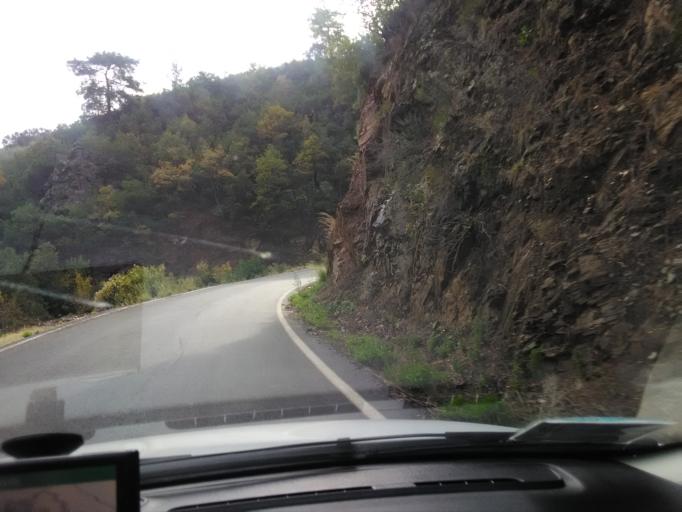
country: TR
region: Antalya
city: Gazipasa
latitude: 36.2519
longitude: 32.3976
